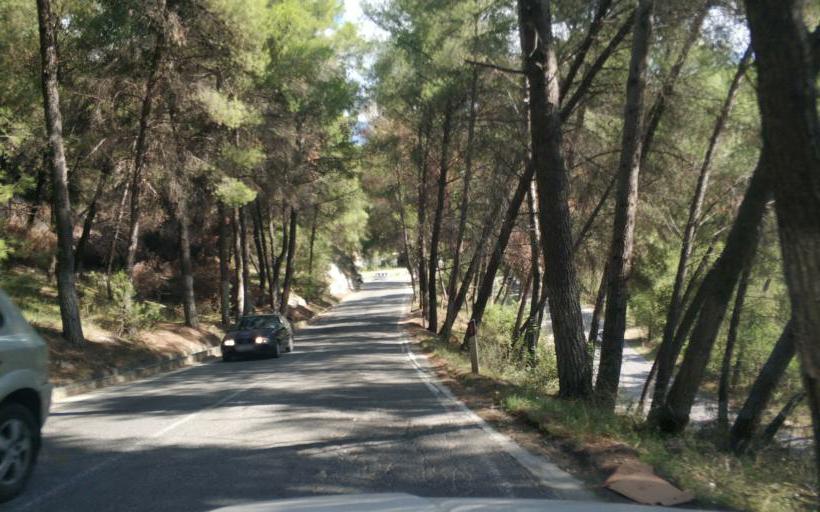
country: AL
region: Durres
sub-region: Rrethi i Krujes
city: Kruje
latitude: 41.4908
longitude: 19.7682
